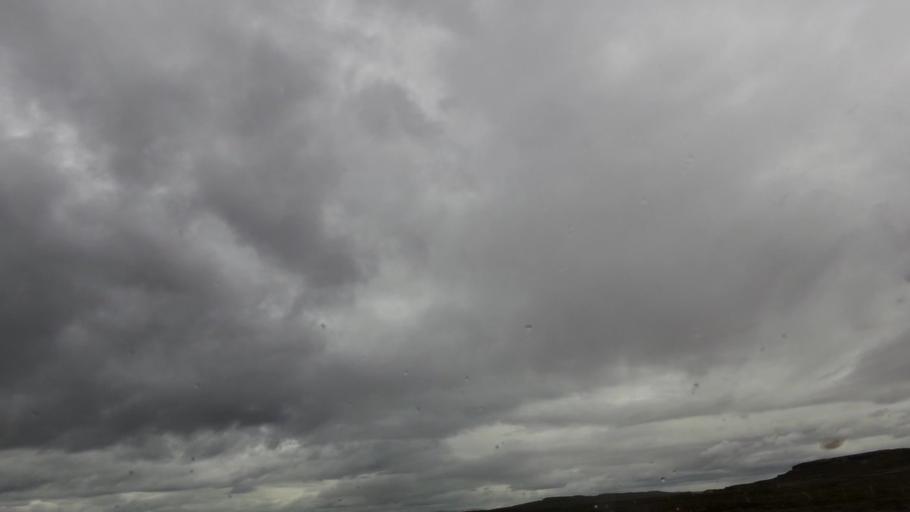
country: IS
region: West
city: Borgarnes
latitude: 65.0252
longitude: -22.1270
